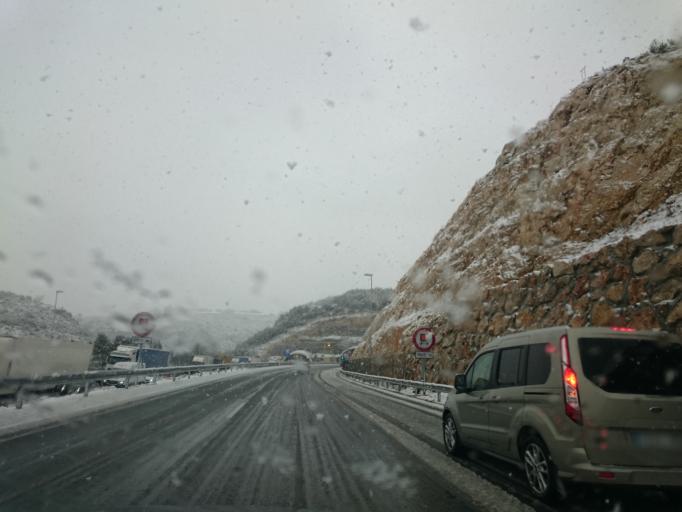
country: ES
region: Catalonia
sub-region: Provincia de Barcelona
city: Vilafranca del Penedes
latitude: 41.3028
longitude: 1.7239
